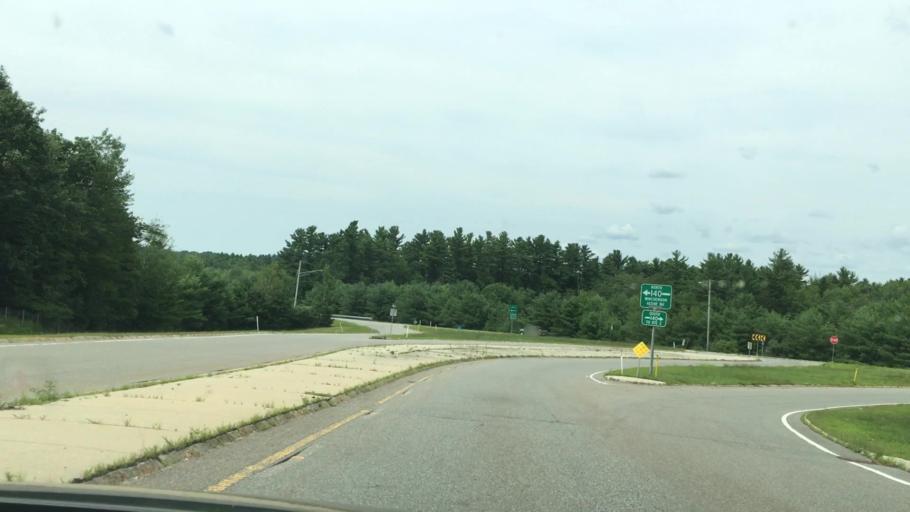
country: US
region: Massachusetts
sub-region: Worcester County
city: Gardner
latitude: 42.6034
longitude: -71.9891
